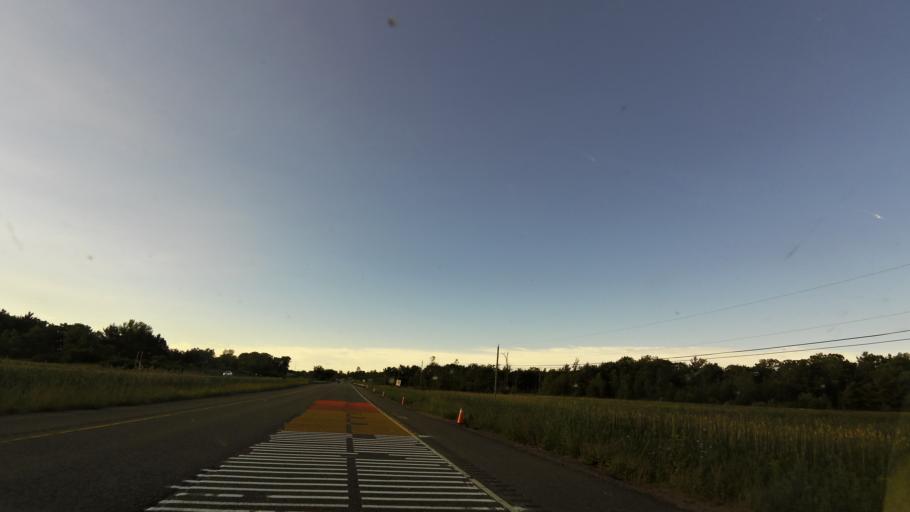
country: CA
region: Ontario
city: Midland
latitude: 44.8222
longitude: -79.7378
